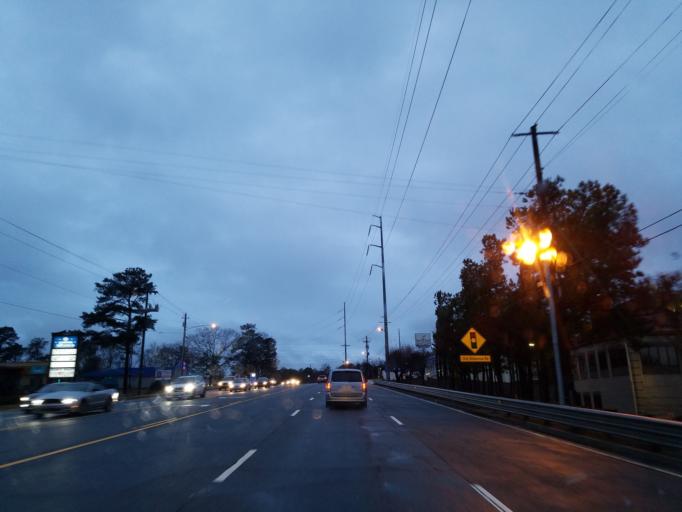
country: US
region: Georgia
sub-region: Fulton County
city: Roswell
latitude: 34.0190
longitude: -84.3142
